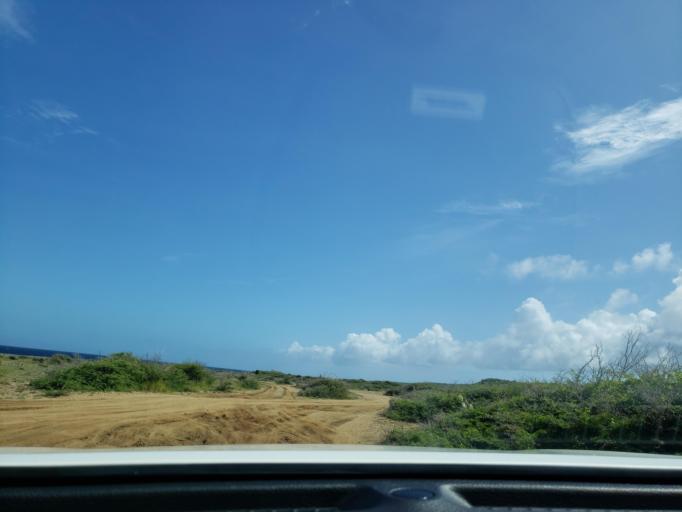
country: CW
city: Barber
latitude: 12.3642
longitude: -69.1109
